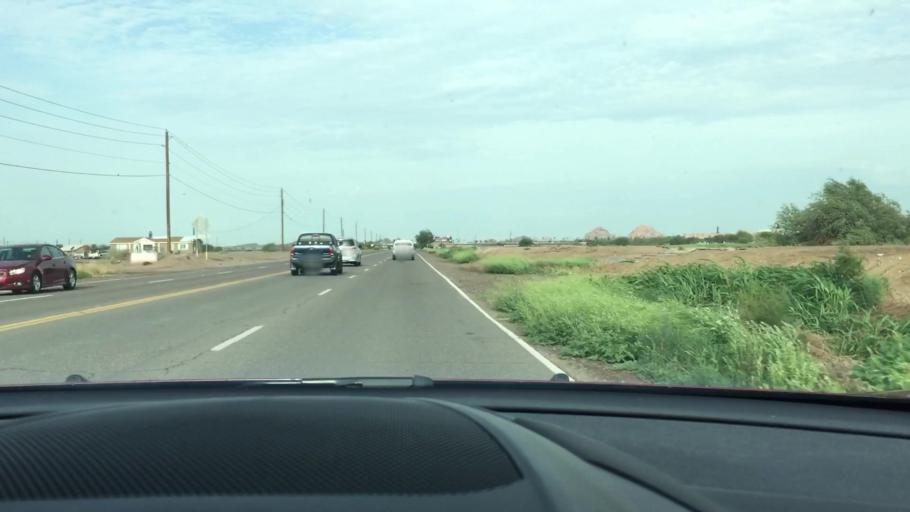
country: US
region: Arizona
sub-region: Maricopa County
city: Tempe
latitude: 33.4508
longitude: -111.8762
